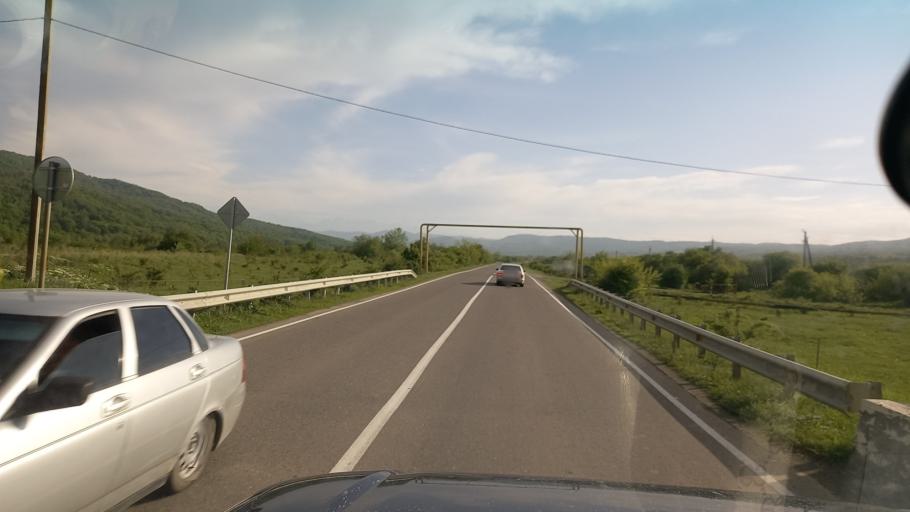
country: RU
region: Ingushetiya
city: Nesterovskaya
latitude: 43.2169
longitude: 45.0264
